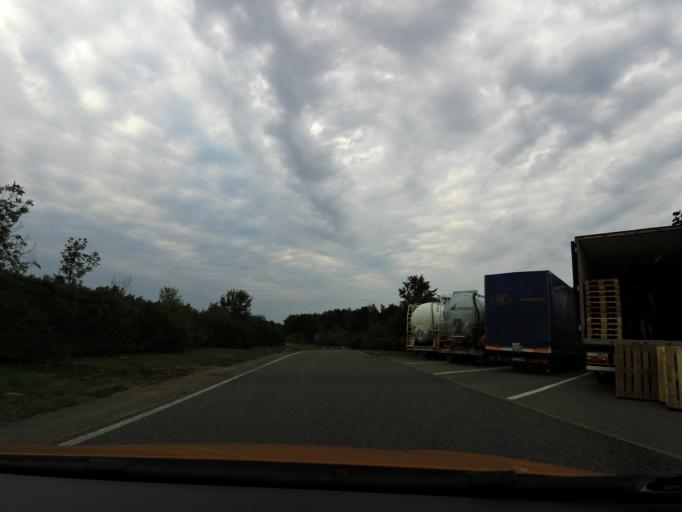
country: DE
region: Berlin
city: Wannsee
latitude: 52.3845
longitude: 13.1535
